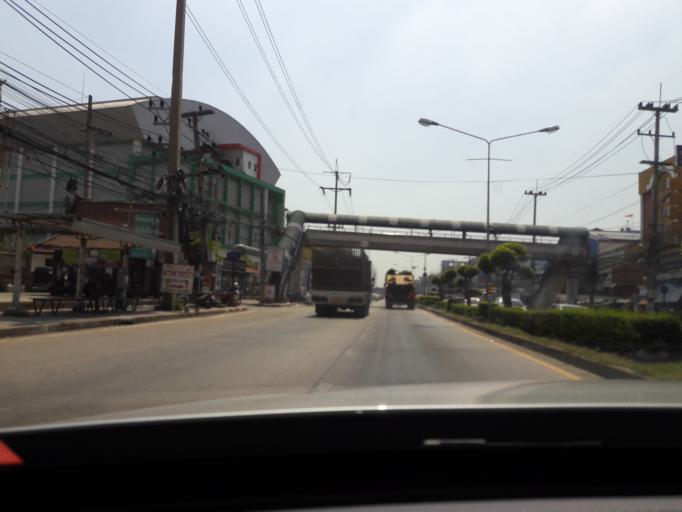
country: TH
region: Samut Sakhon
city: Samut Sakhon
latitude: 13.5721
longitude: 100.2727
